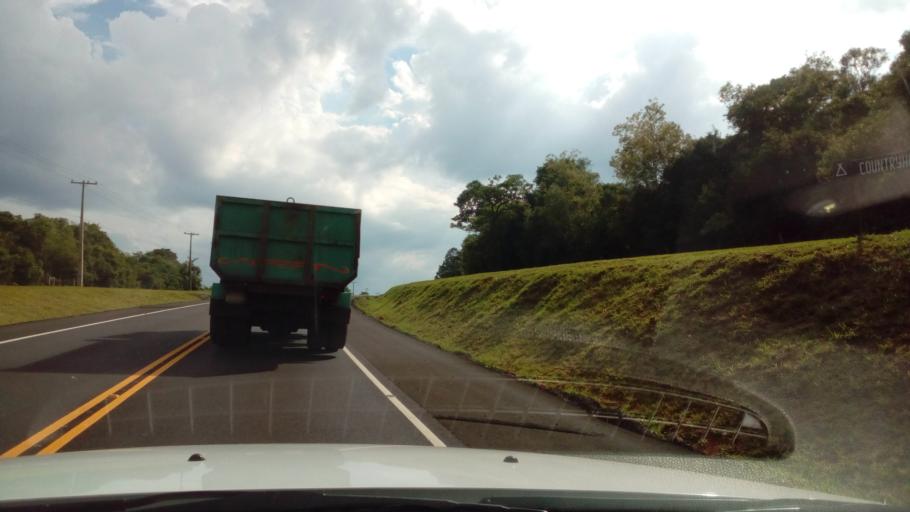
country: PY
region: Itapua
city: Trinidad
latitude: -27.1479
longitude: -55.7544
